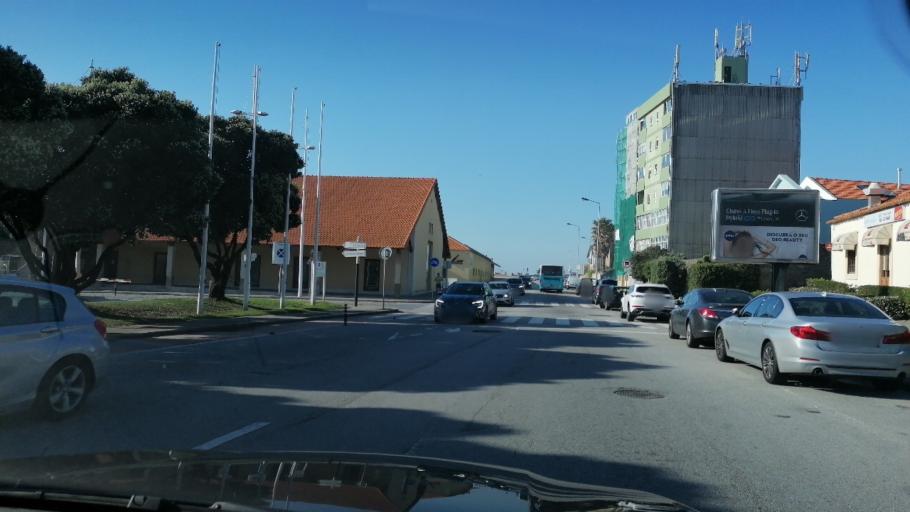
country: PT
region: Porto
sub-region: Matosinhos
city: Leca da Palmeira
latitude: 41.1880
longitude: -8.7031
